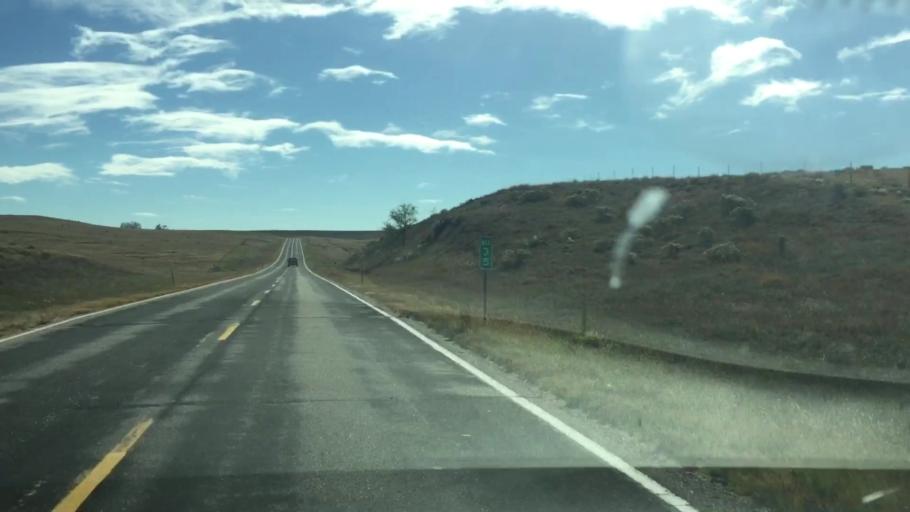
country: US
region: Colorado
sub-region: Elbert County
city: Kiowa
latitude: 39.2761
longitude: -104.2598
